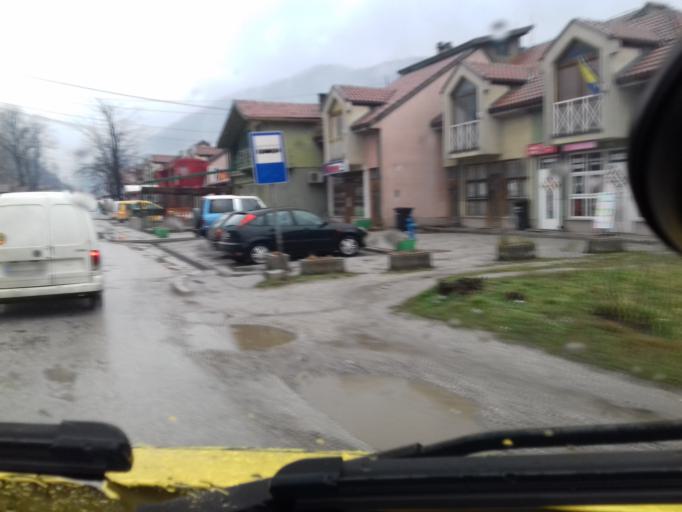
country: BA
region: Federation of Bosnia and Herzegovina
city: Zeljezno Polje
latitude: 44.3298
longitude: 17.9131
